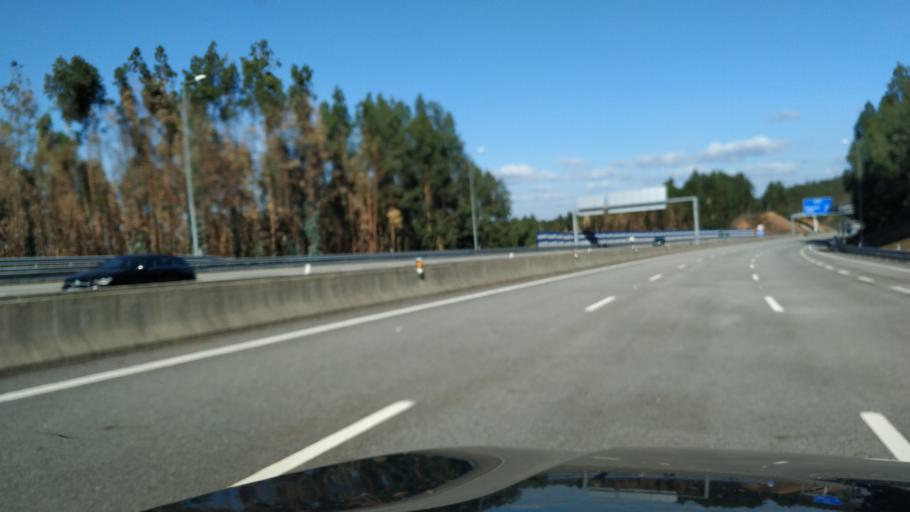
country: PT
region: Aveiro
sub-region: Santa Maria da Feira
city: Lobao
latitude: 41.0183
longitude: -8.4787
